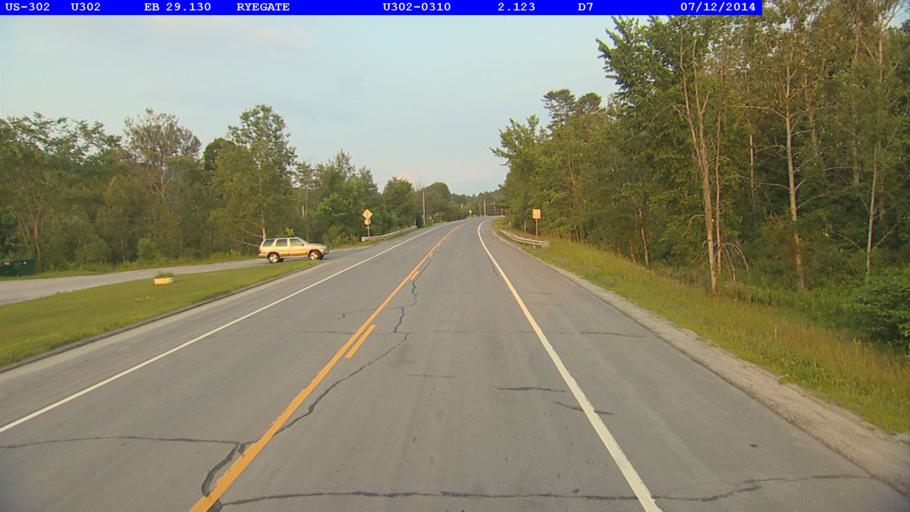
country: US
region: New Hampshire
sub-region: Grafton County
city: Woodsville
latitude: 44.1867
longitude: -72.1396
